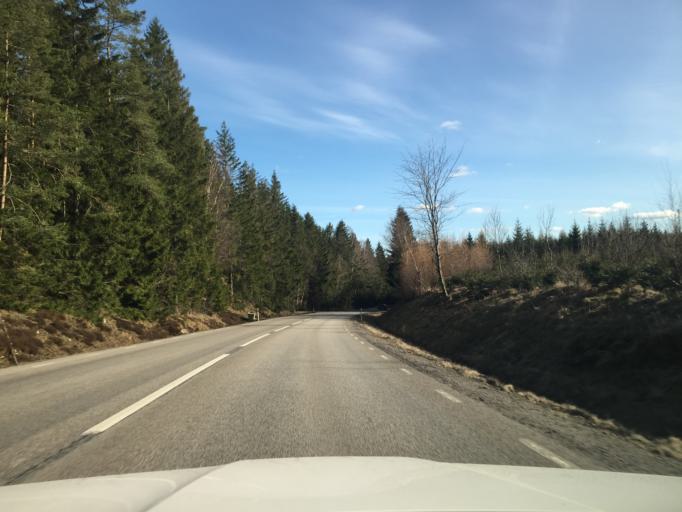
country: SE
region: Vaestra Goetaland
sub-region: Marks Kommun
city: Horred
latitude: 57.1566
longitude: 12.6691
